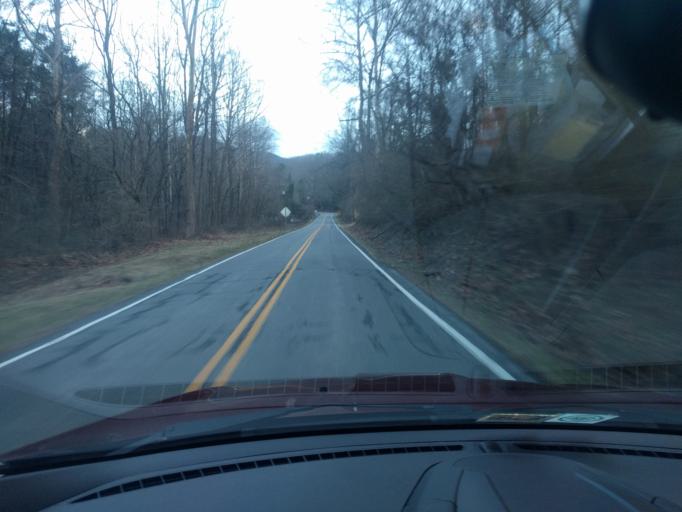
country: US
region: Virginia
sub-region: Botetourt County
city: Buchanan
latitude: 37.5169
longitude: -79.6662
